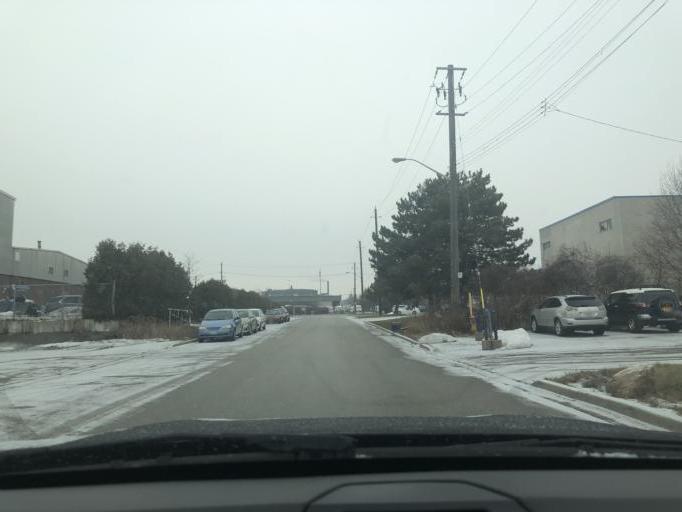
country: CA
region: Ontario
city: Scarborough
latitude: 43.7724
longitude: -79.2695
